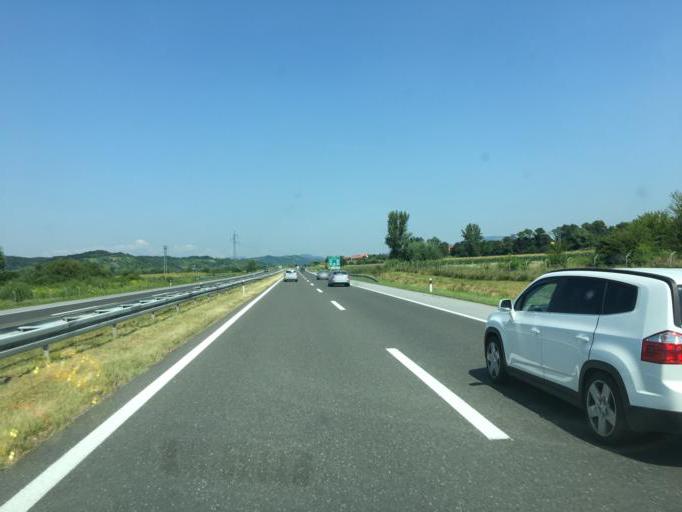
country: HR
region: Krapinsko-Zagorska
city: Zabok
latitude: 46.0468
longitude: 15.9239
